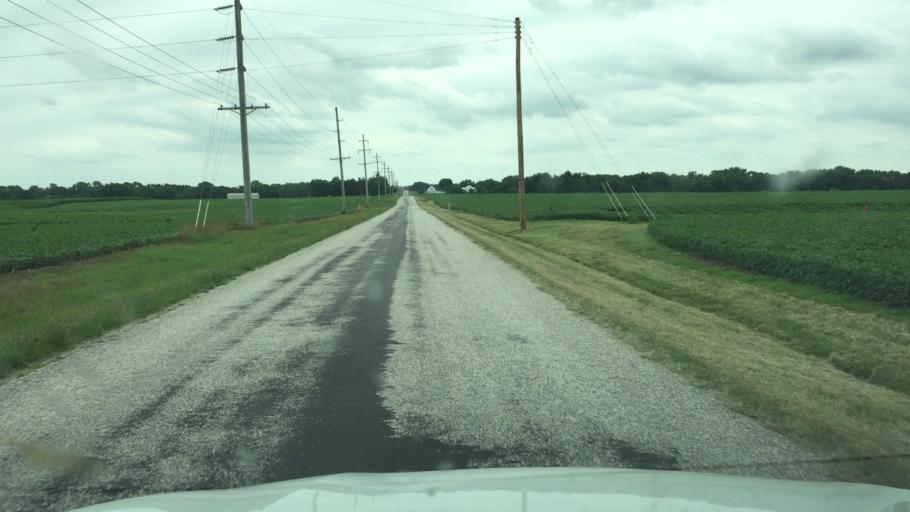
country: US
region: Illinois
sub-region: Hancock County
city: Carthage
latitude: 40.3076
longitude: -91.0830
